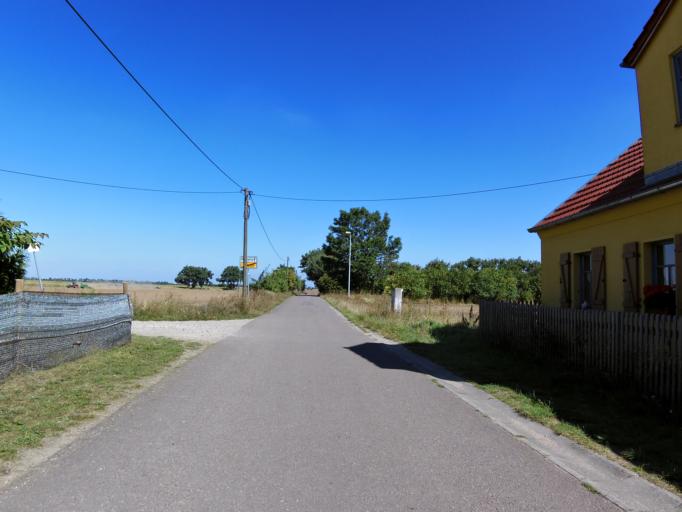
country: DE
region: Brandenburg
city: Muhlberg
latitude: 51.3951
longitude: 13.2453
